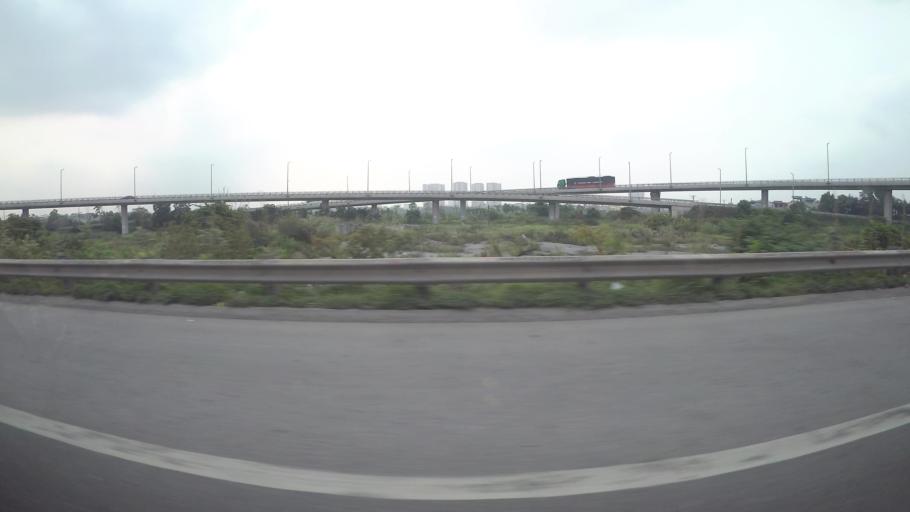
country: VN
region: Ha Noi
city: Trau Quy
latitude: 21.0126
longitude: 105.9179
